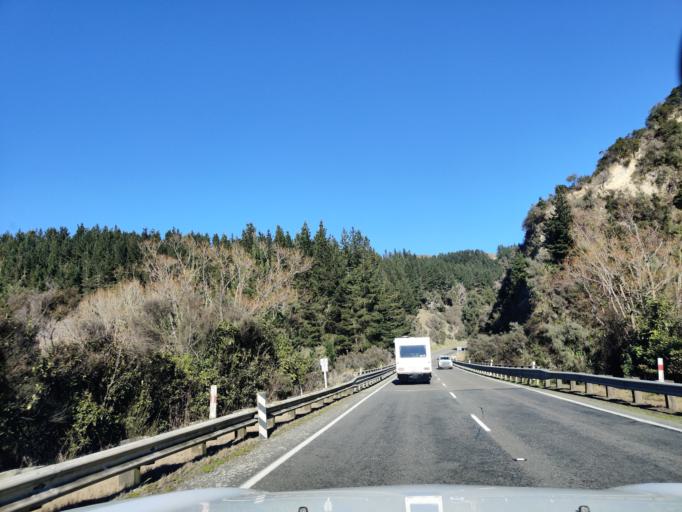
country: NZ
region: Manawatu-Wanganui
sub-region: Ruapehu District
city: Waiouru
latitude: -39.7587
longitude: 175.8271
